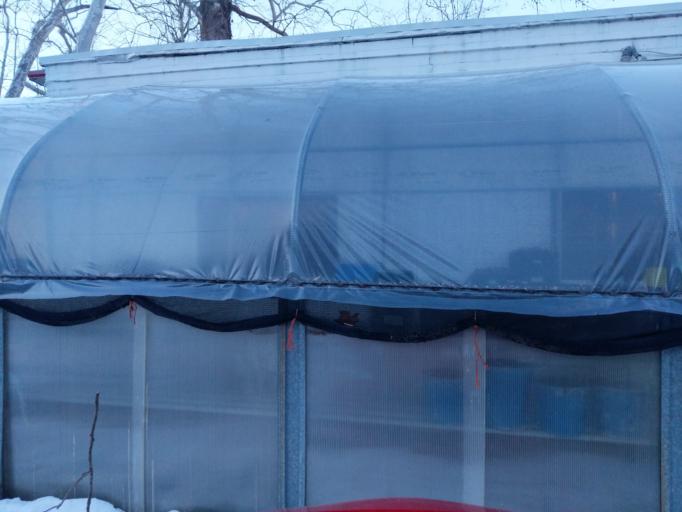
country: US
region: Ohio
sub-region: Athens County
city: Athens
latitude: 39.3298
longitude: -82.1256
